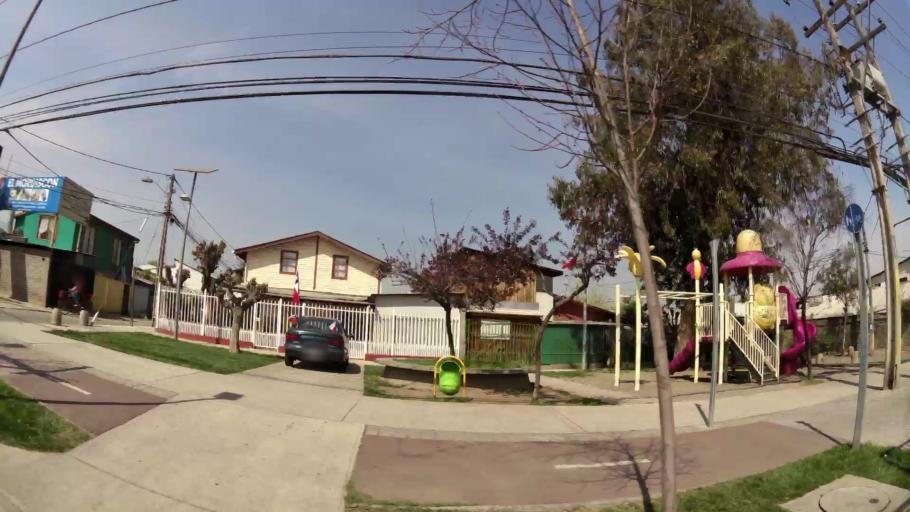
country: CL
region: Santiago Metropolitan
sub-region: Provincia de Santiago
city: Villa Presidente Frei, Nunoa, Santiago, Chile
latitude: -33.5105
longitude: -70.5826
